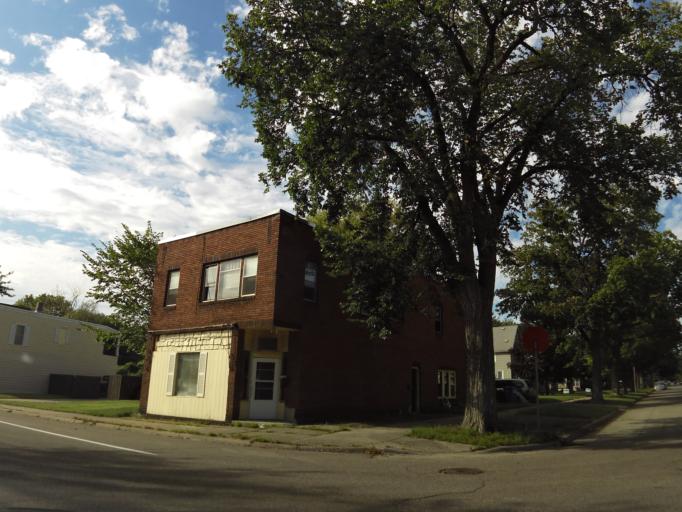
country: US
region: Minnesota
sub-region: Hennepin County
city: Saint Anthony
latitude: 45.0132
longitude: -93.2438
